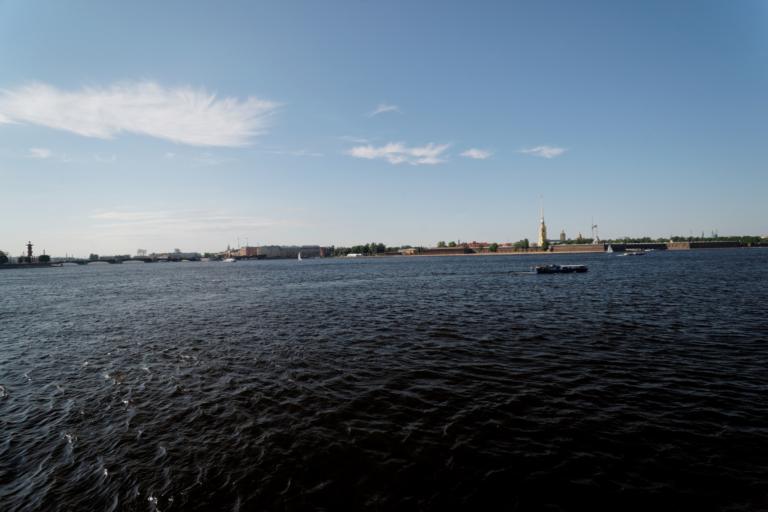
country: RU
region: St.-Petersburg
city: Saint Petersburg
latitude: 59.9427
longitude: 30.3170
